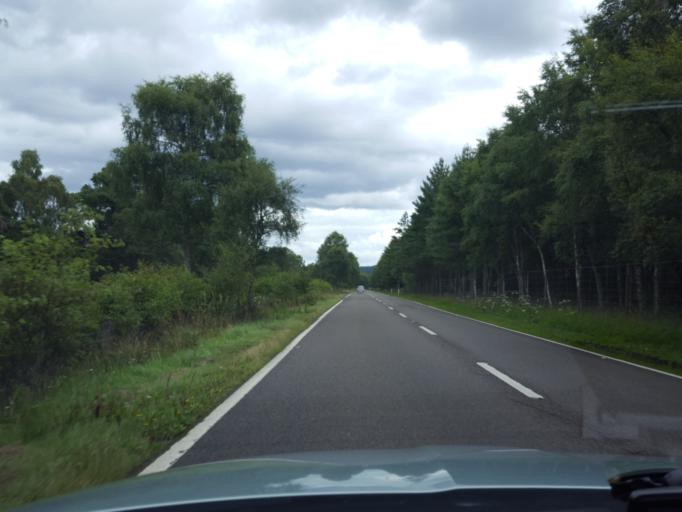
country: GB
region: Scotland
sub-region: Highland
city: Grantown on Spey
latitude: 57.3676
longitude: -3.5062
